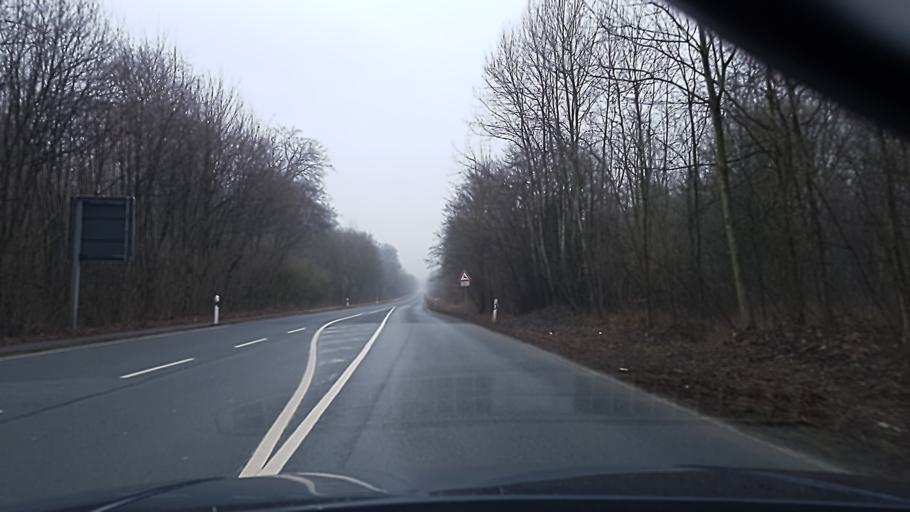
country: DE
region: Lower Saxony
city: Cramme
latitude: 52.1685
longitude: 10.4390
